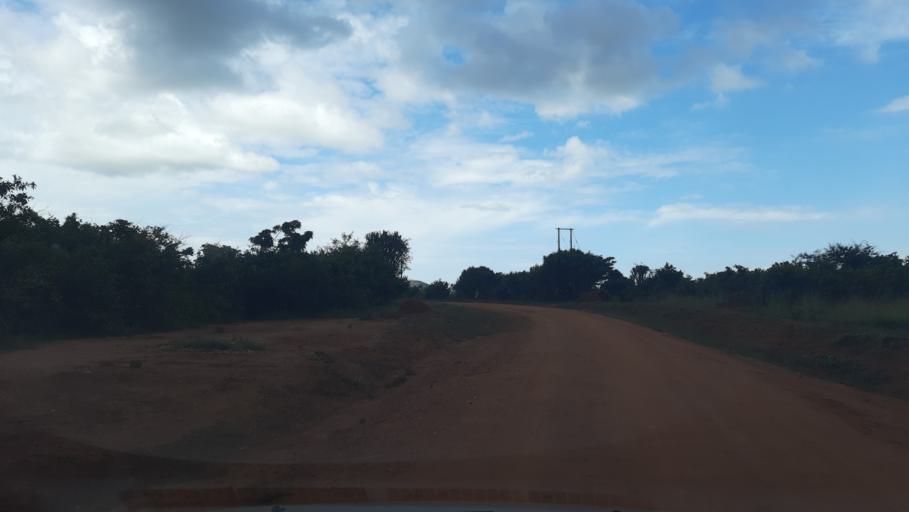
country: UG
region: Central Region
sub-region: Nakasongola District
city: Nakasongola
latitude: 1.3725
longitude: 32.4826
